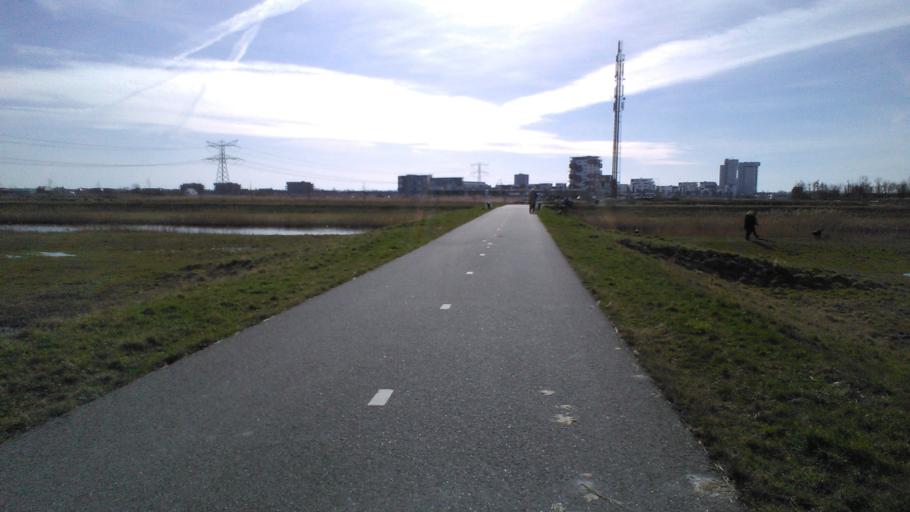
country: NL
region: South Holland
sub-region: Gemeente Lansingerland
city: Bleiswijk
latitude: 51.9916
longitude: 4.5801
